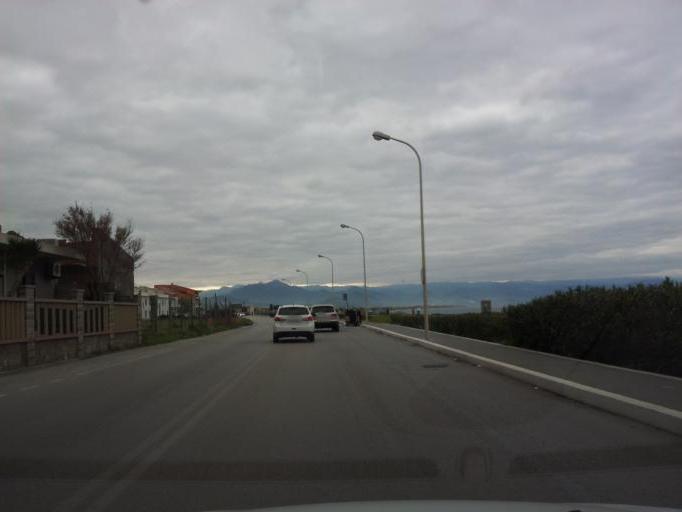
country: IT
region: Sicily
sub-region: Messina
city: Milazzo
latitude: 38.2086
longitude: 15.2285
